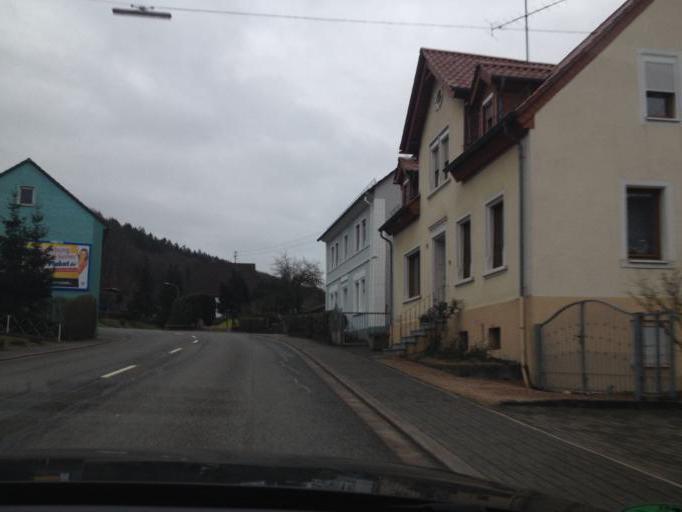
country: DE
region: Saarland
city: Nohfelden
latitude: 49.5864
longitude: 7.1472
